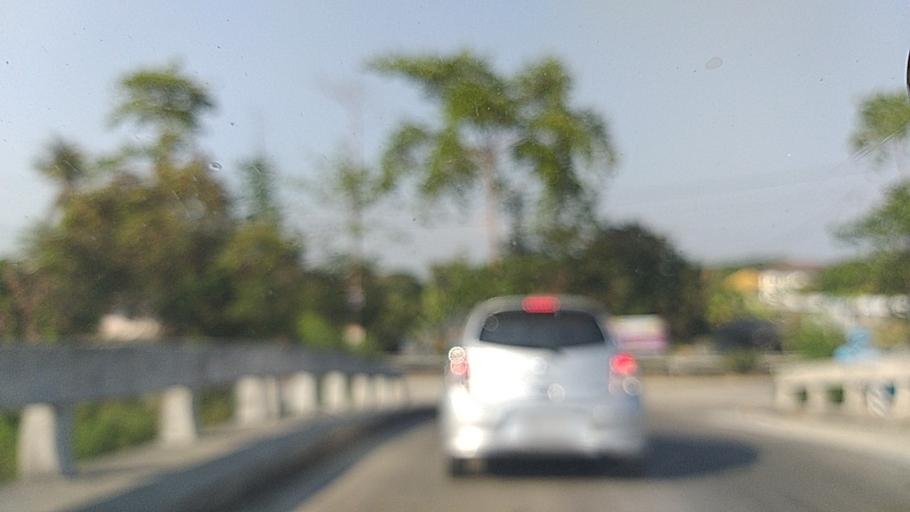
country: TH
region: Nonthaburi
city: Bang Bua Thong
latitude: 13.9349
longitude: 100.3795
